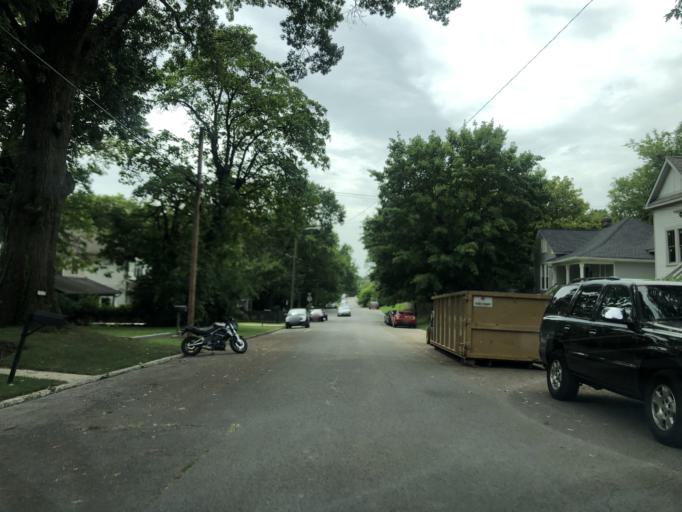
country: US
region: Tennessee
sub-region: Davidson County
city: Nashville
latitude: 36.1681
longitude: -86.7383
